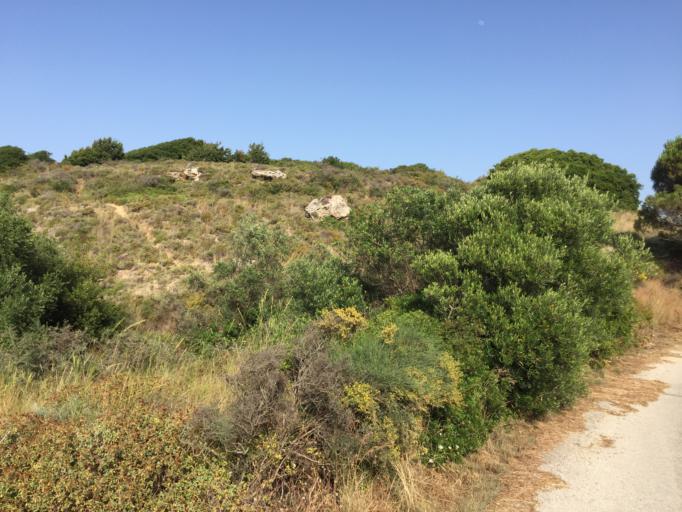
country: GR
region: Ionian Islands
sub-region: Nomos Zakynthou
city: Vanaton
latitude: 37.8261
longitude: 20.8587
